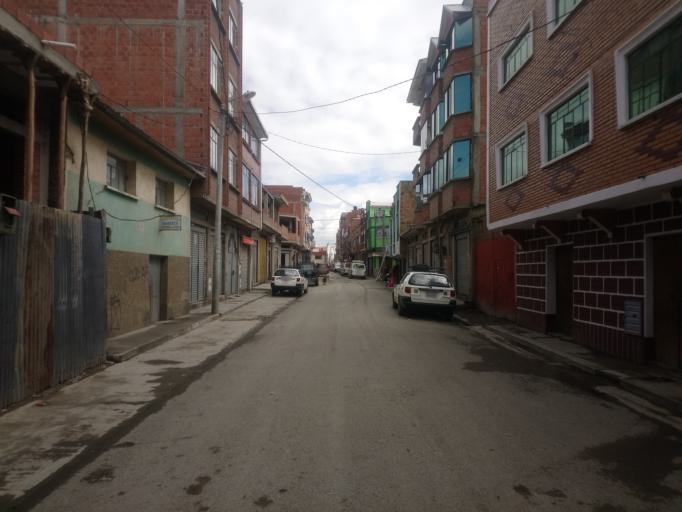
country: BO
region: La Paz
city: Achacachi
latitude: -16.0459
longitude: -68.6847
